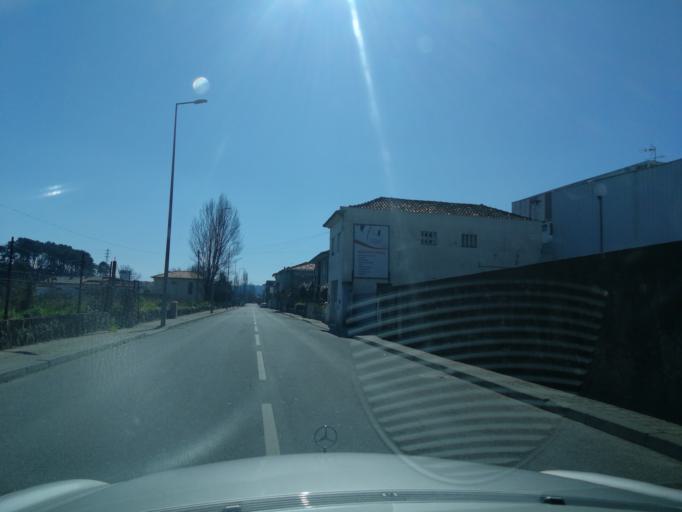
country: PT
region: Braga
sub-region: Vila Nova de Famalicao
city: Vila Nova de Famalicao
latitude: 41.3999
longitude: -8.5202
